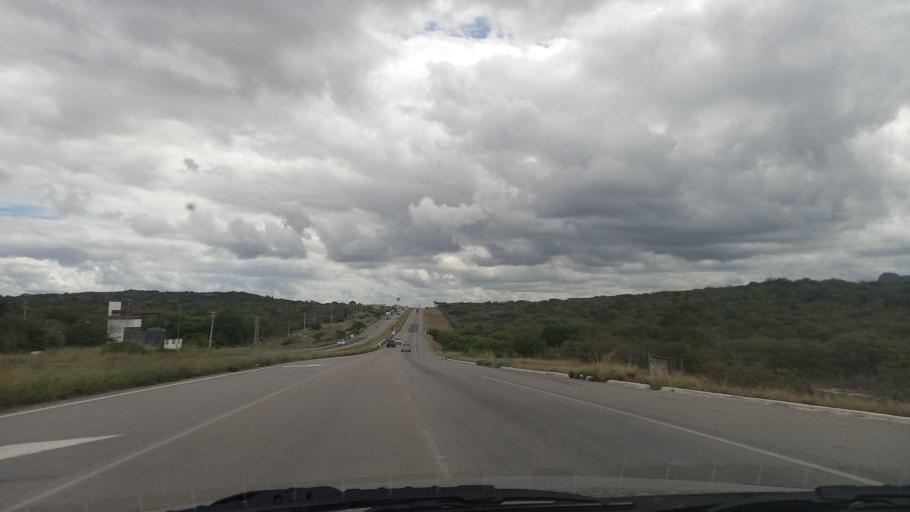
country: BR
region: Pernambuco
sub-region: Caruaru
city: Caruaru
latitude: -8.3196
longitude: -36.0696
